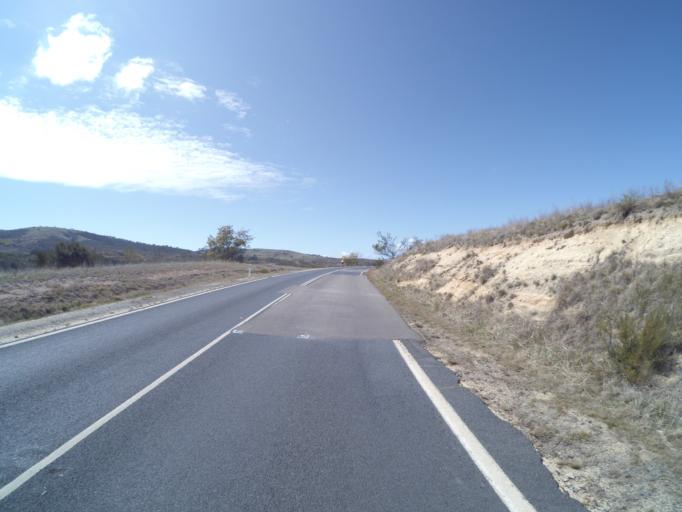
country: AU
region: Australian Capital Territory
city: Macarthur
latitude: -35.4513
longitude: 148.9998
